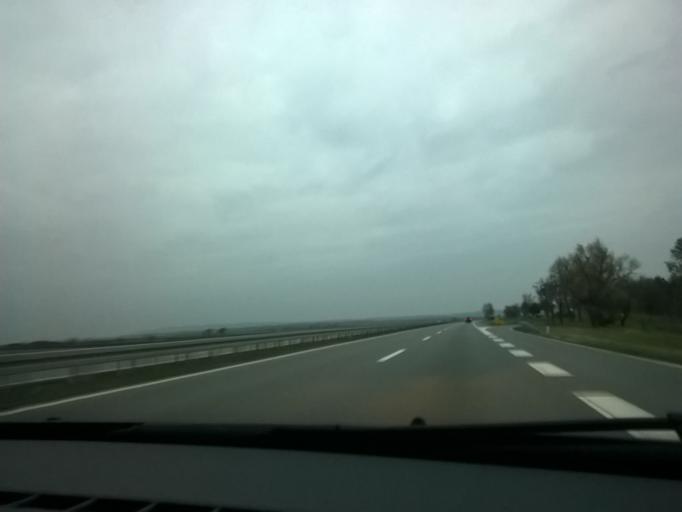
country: RS
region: Autonomna Pokrajina Vojvodina
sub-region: Juznobacki Okrug
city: Kovilj
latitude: 45.2187
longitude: 20.0619
